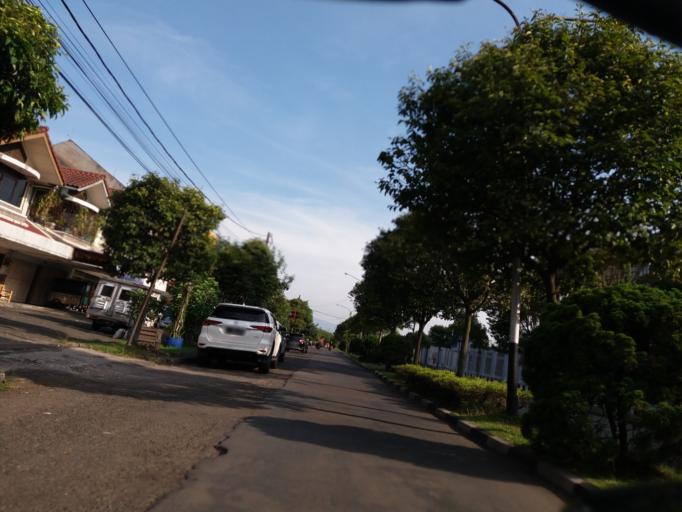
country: ID
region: West Java
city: Bandung
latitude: -6.9569
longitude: 107.6239
